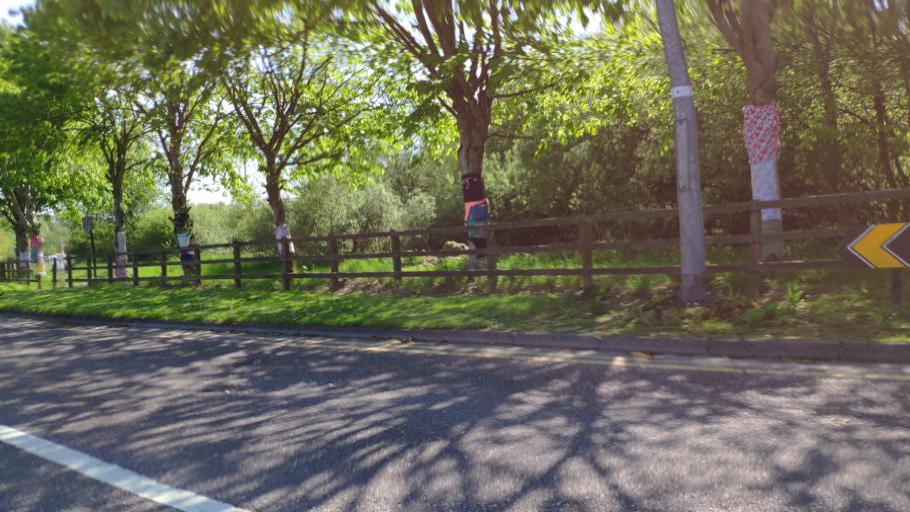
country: IE
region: Munster
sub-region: County Cork
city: Blarney
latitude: 51.9283
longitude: -8.5572
